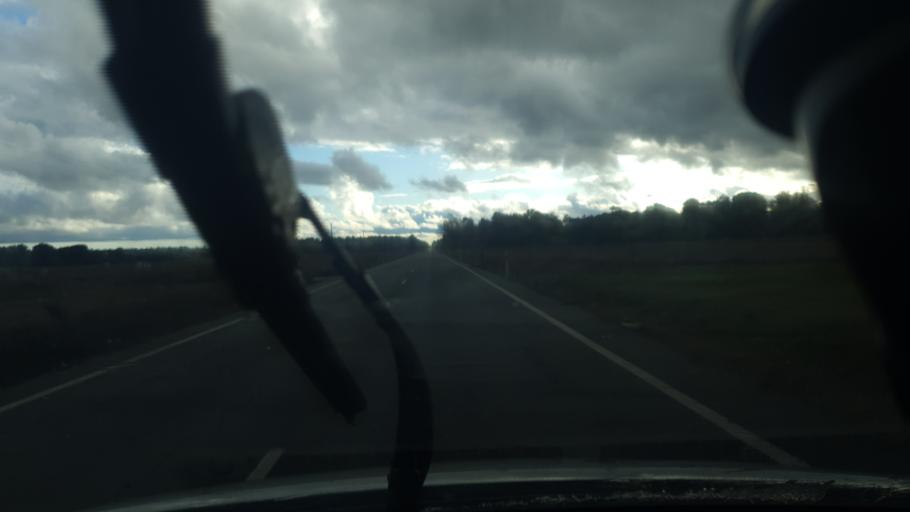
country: ES
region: Castille and Leon
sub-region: Provincia de Segovia
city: Samboal
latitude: 41.2820
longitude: -4.4137
